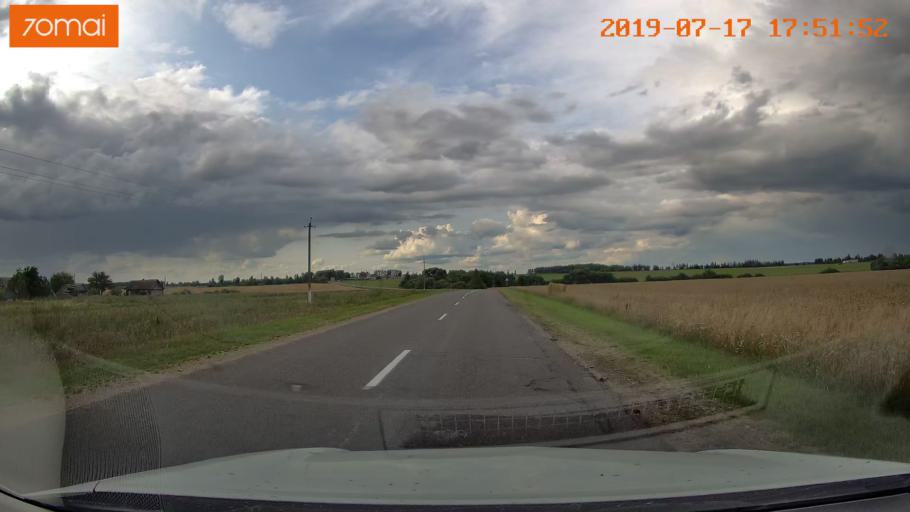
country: BY
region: Mogilev
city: Hlusha
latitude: 53.1581
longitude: 28.7872
